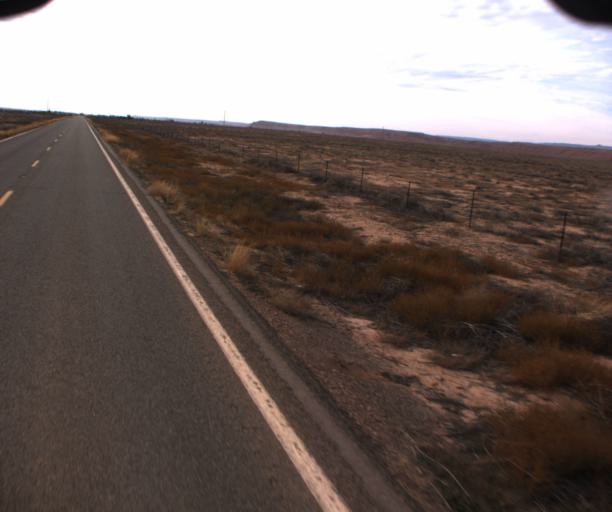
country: US
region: Arizona
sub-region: Apache County
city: Many Farms
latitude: 36.4479
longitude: -109.6077
